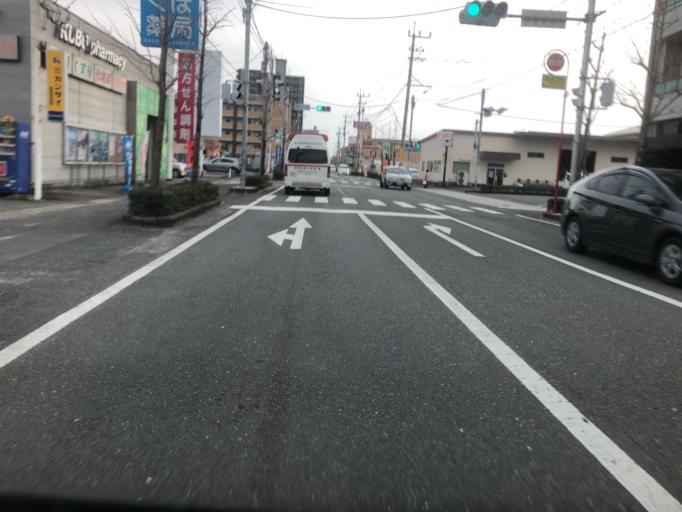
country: JP
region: Saga Prefecture
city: Saga-shi
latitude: 33.2807
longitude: 130.2696
